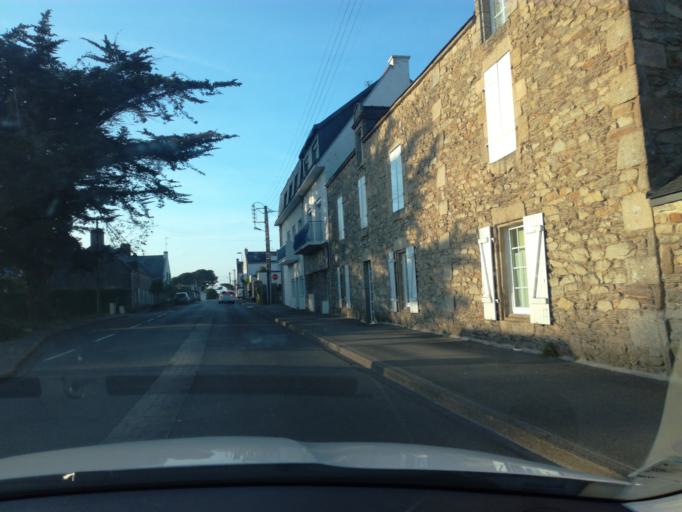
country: FR
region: Brittany
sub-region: Departement du Morbihan
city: Saint-Pierre-Quiberon
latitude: 47.5354
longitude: -3.1349
